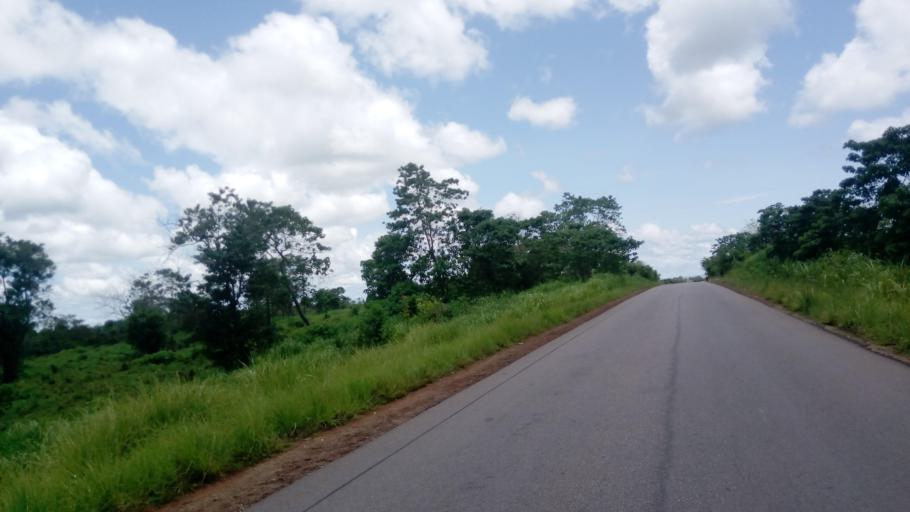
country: SL
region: Northern Province
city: Binkolo
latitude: 8.9307
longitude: -12.0065
